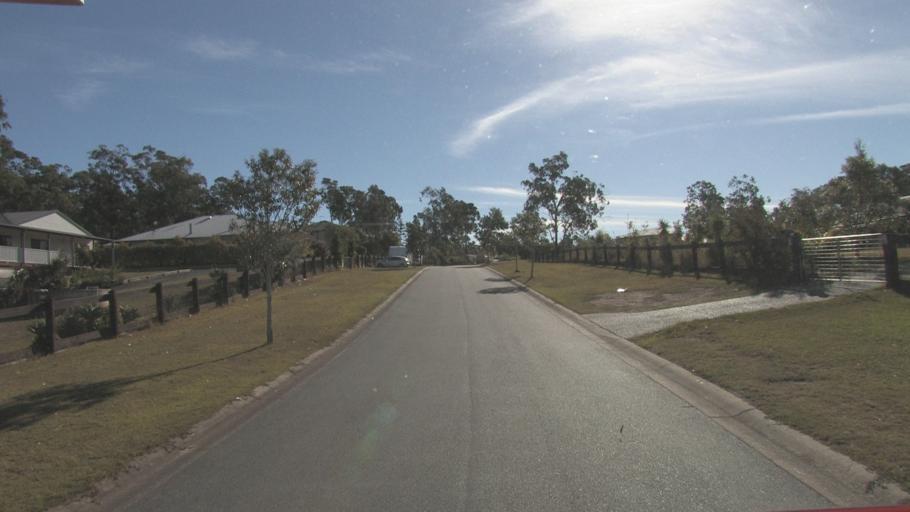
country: AU
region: Queensland
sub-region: Ipswich
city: Springfield Lakes
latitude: -27.7206
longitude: 152.9219
